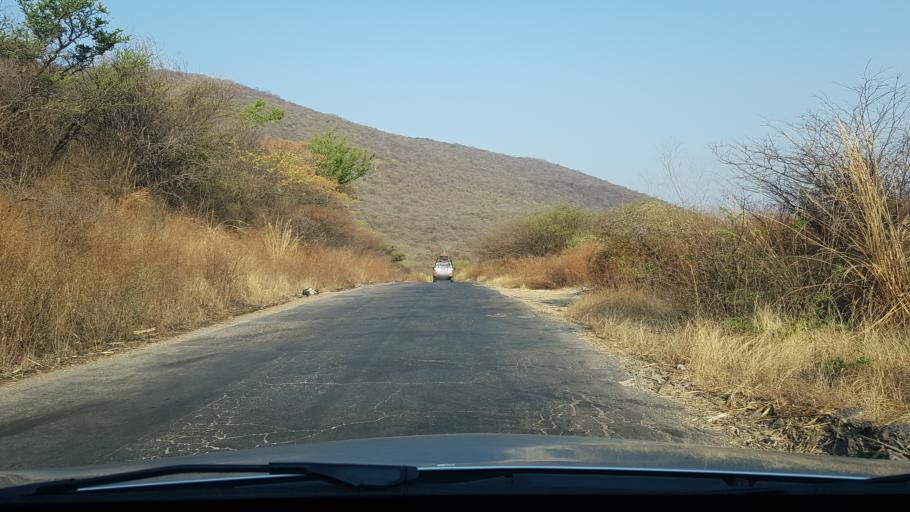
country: MX
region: Morelos
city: Tlaltizapan
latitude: 18.6638
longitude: -99.0481
